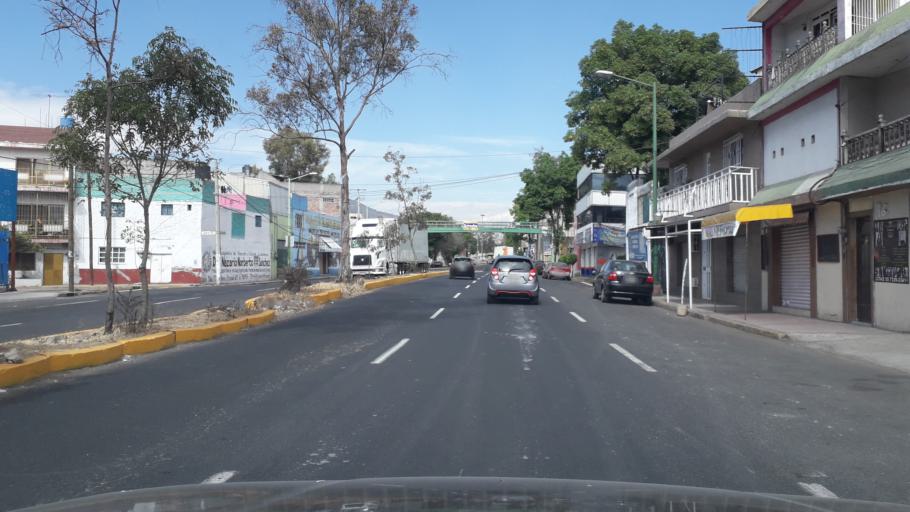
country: MX
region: Mexico City
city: Gustavo A. Madero
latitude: 19.5032
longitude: -99.0905
